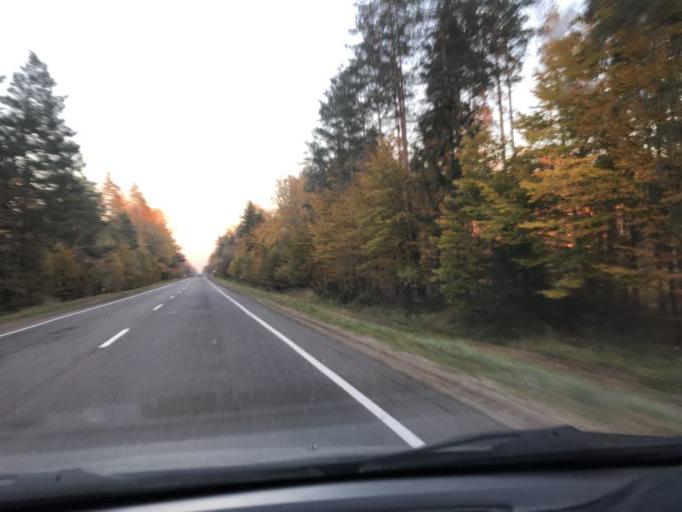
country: BY
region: Mogilev
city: Hlusha
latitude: 53.0892
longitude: 28.8834
